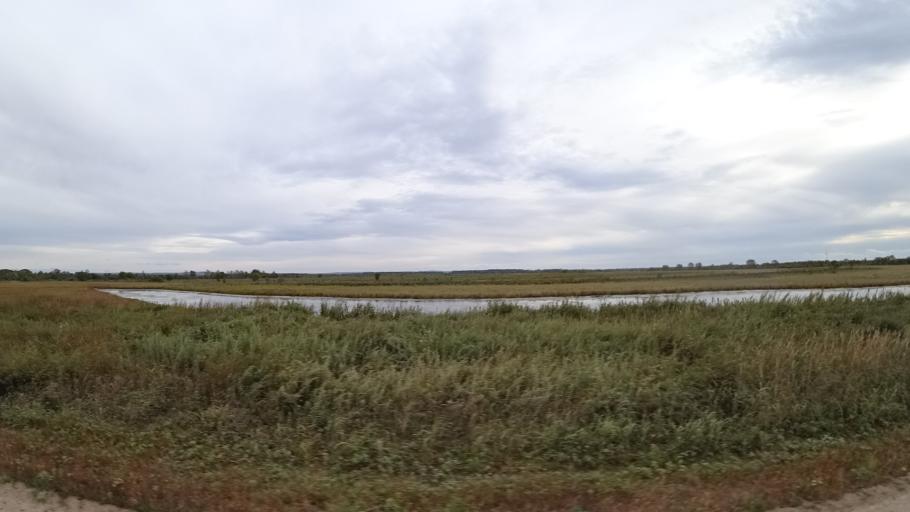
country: RU
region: Amur
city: Arkhara
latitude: 49.4305
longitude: 130.2392
